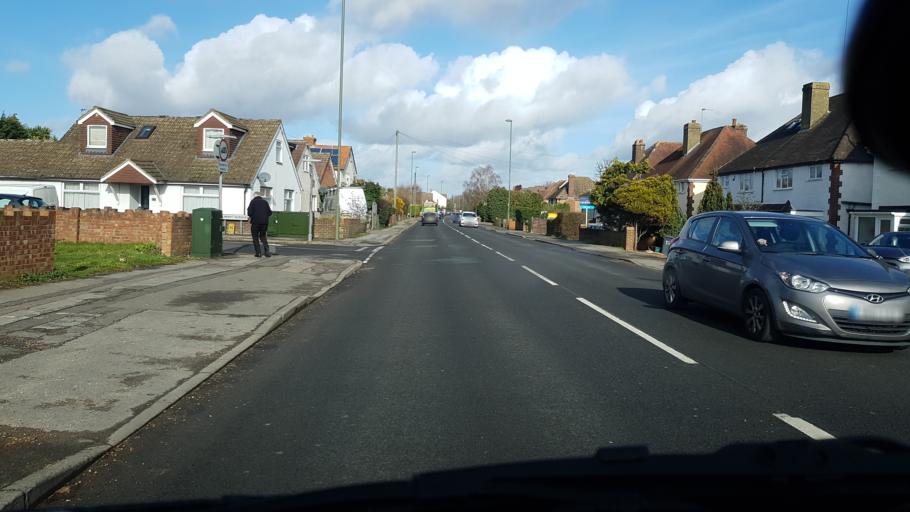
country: GB
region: England
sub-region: Surrey
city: Guildford
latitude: 51.2572
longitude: -0.5946
